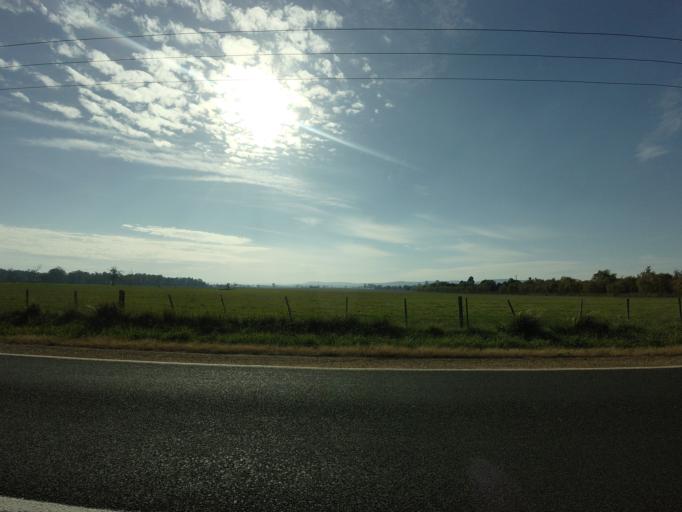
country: AU
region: Tasmania
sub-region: Northern Midlands
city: Longford
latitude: -41.5305
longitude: 146.9905
